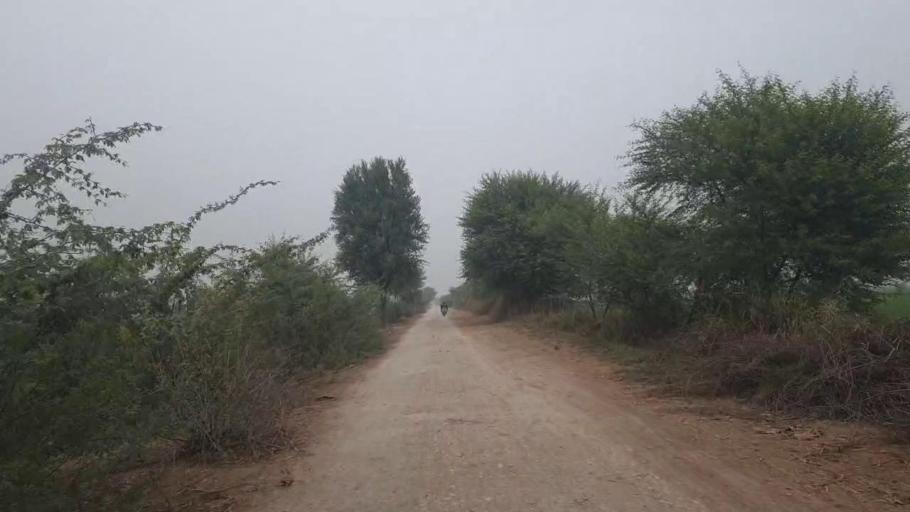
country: PK
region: Sindh
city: Tando Adam
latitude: 25.7710
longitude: 68.6985
